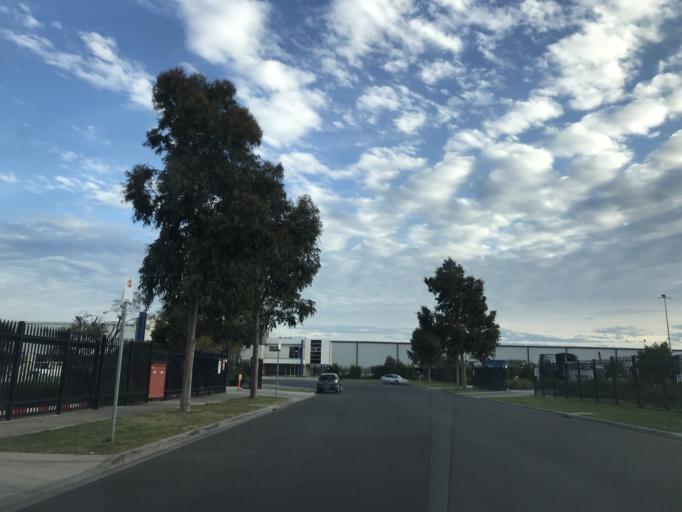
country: AU
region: Victoria
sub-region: Brimbank
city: Derrimut
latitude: -37.8050
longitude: 144.7618
